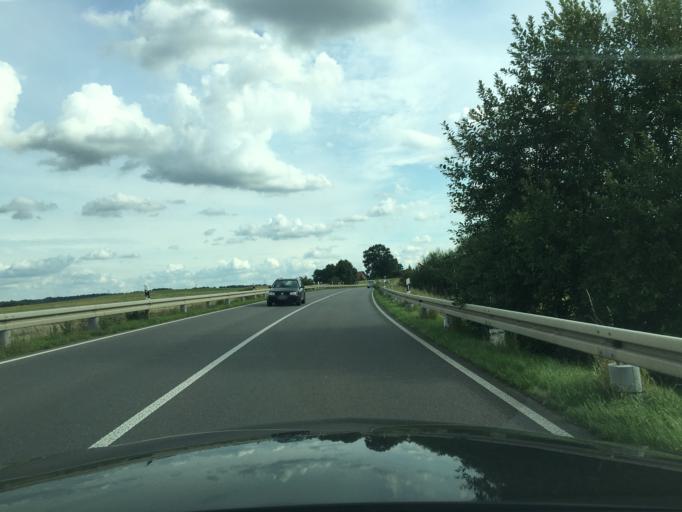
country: DE
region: Mecklenburg-Vorpommern
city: Penzlin
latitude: 53.4894
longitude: 13.0725
